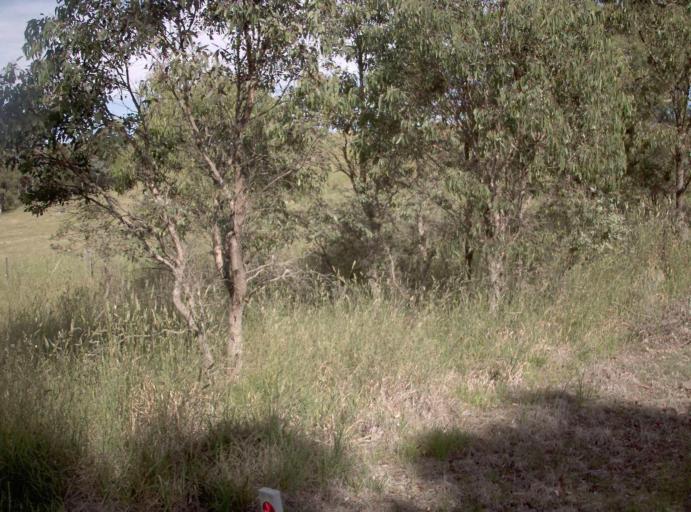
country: AU
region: Victoria
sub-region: East Gippsland
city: Lakes Entrance
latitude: -37.4950
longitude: 148.1332
